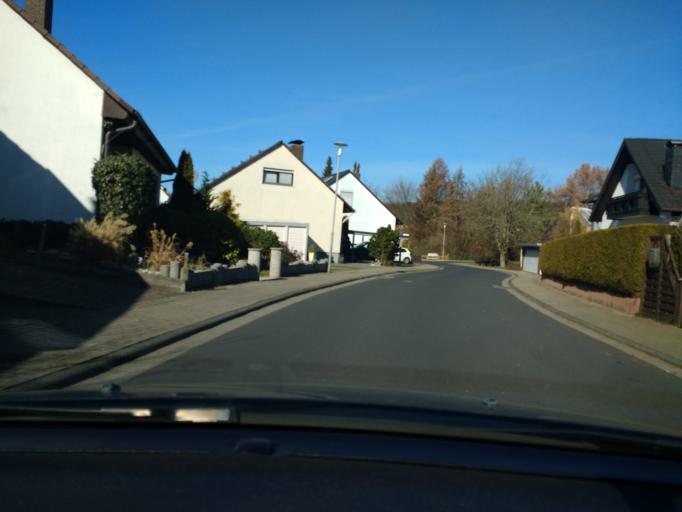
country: DE
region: Hesse
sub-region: Regierungsbezirk Darmstadt
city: Rodenbach
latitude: 50.1378
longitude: 9.0631
